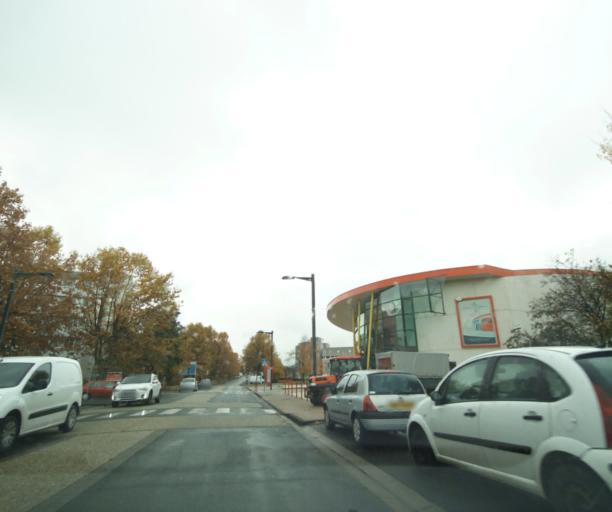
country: FR
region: Auvergne
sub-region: Departement du Puy-de-Dome
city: Cournon-d'Auvergne
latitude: 45.7309
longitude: 3.1911
